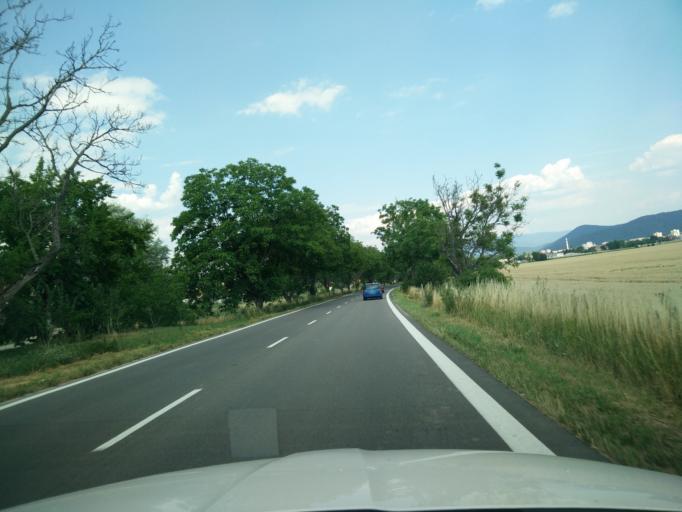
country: SK
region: Nitriansky
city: Partizanske
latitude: 48.6309
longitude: 18.3246
